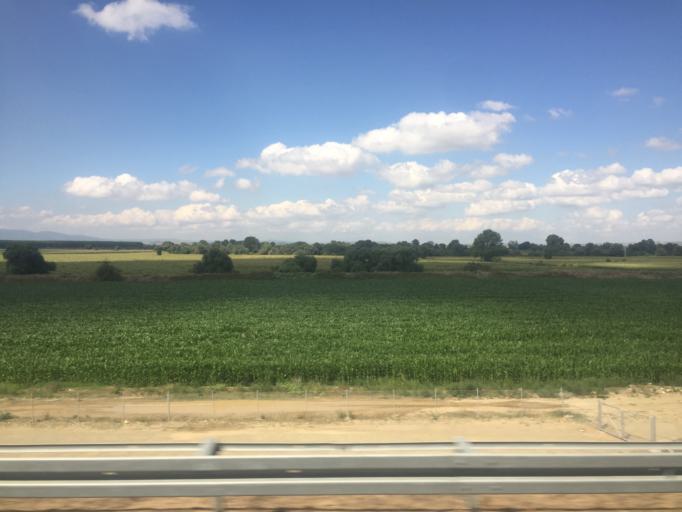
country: TR
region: Bursa
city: Tatkavakli
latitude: 40.1074
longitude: 28.2773
